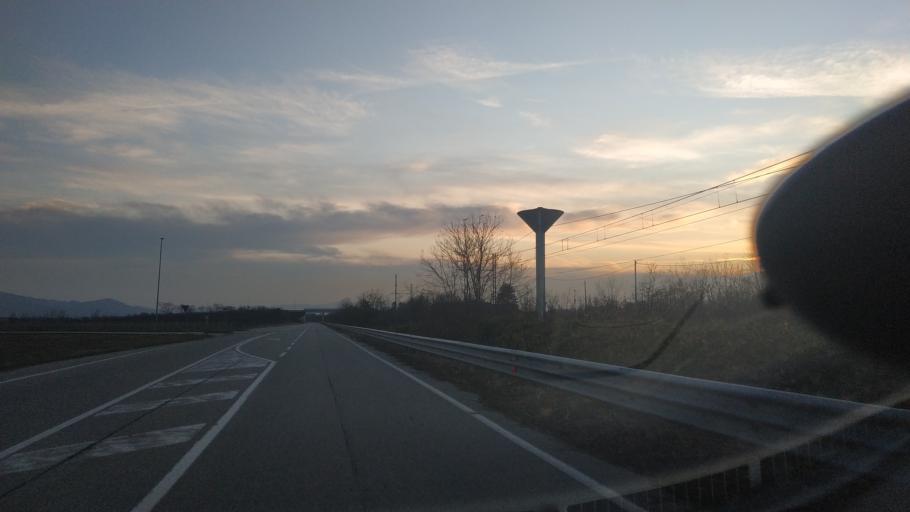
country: IT
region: Piedmont
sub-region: Provincia di Torino
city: Montanaro
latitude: 45.2462
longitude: 7.8631
